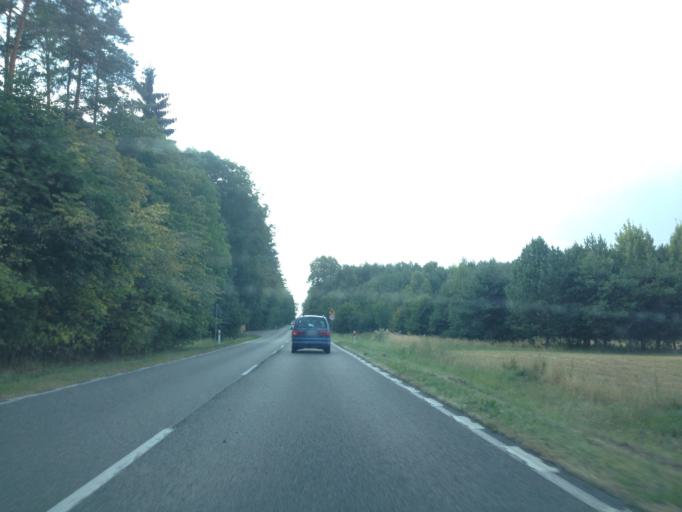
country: PL
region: Kujawsko-Pomorskie
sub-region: Powiat swiecki
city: Lniano
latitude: 53.4734
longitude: 18.1565
